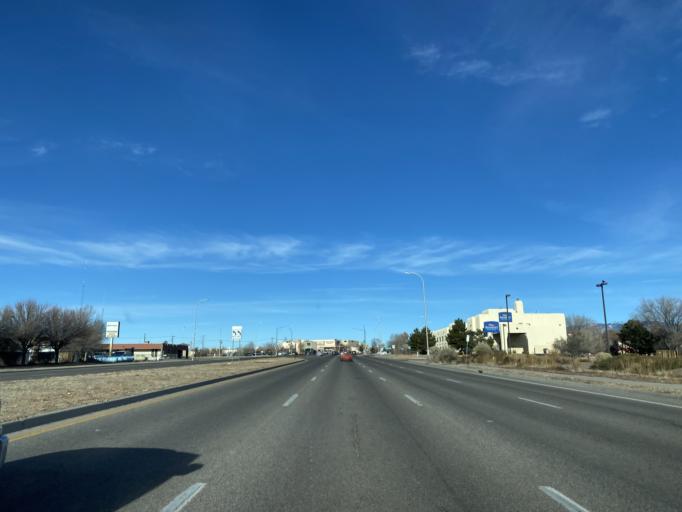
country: US
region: New Mexico
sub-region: Santa Fe County
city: Agua Fria
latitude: 35.6368
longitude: -106.0186
